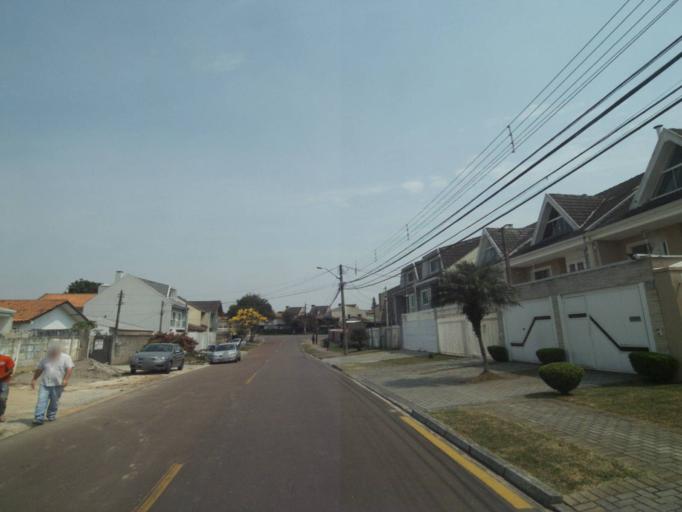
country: BR
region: Parana
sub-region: Sao Jose Dos Pinhais
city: Sao Jose dos Pinhais
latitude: -25.4926
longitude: -49.2107
